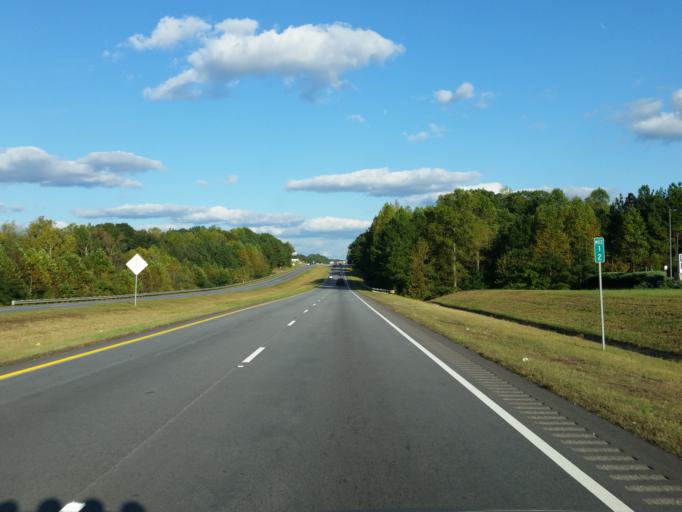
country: US
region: Georgia
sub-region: Paulding County
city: Dallas
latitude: 33.9025
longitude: -84.8001
